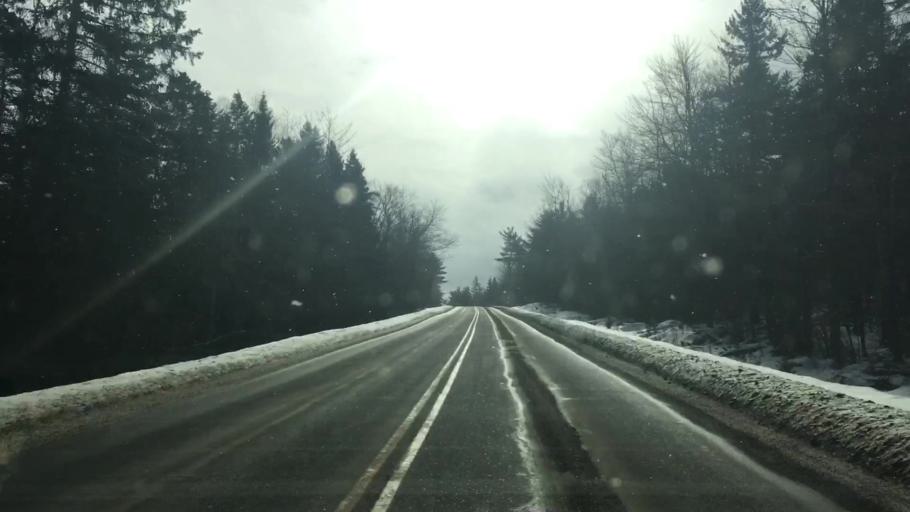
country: US
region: Maine
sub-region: Washington County
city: Calais
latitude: 45.0673
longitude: -67.3306
